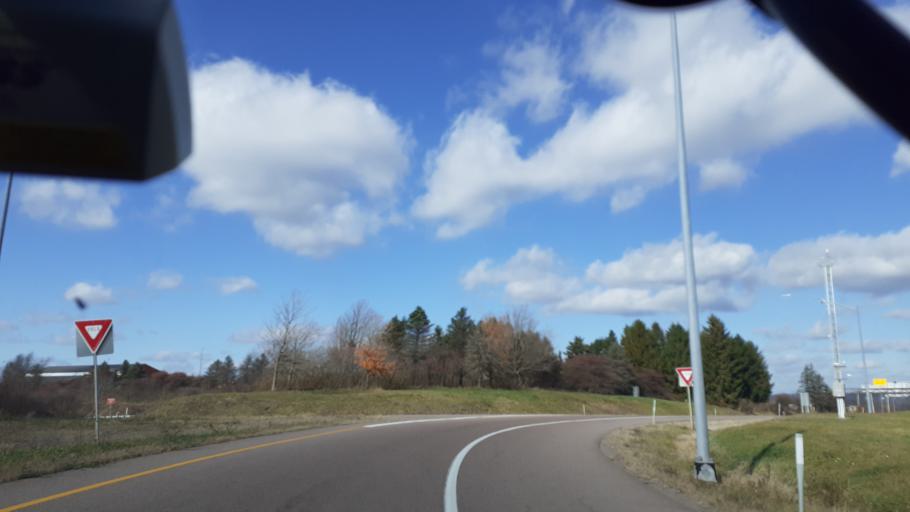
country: US
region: Pennsylvania
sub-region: Somerset County
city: Meyersdale
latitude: 39.6917
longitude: -79.2483
